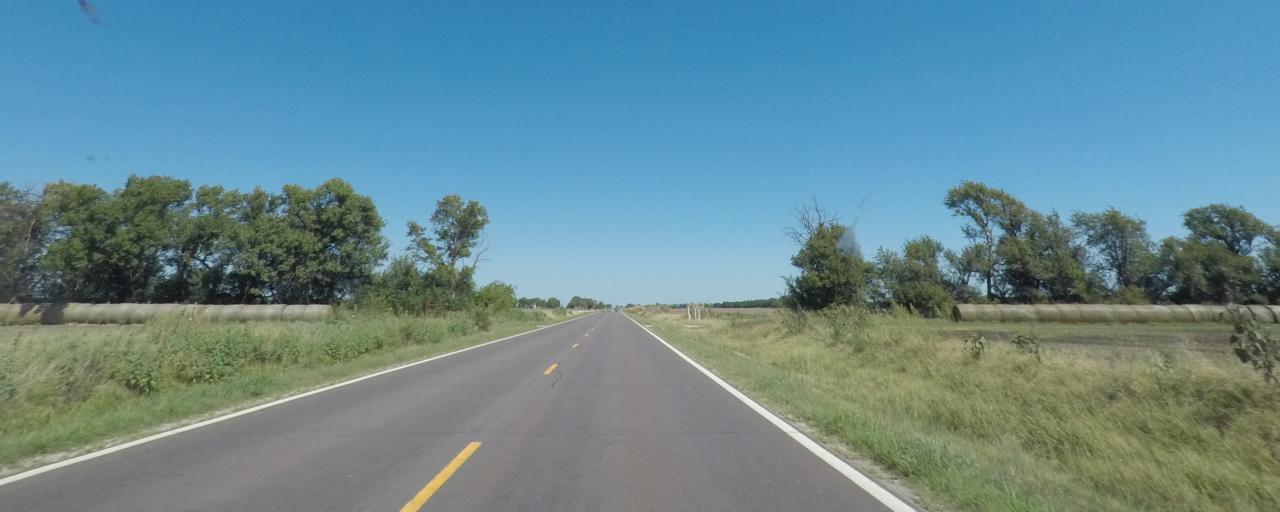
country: US
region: Kansas
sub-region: Sumner County
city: Wellington
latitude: 37.1508
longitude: -97.4023
